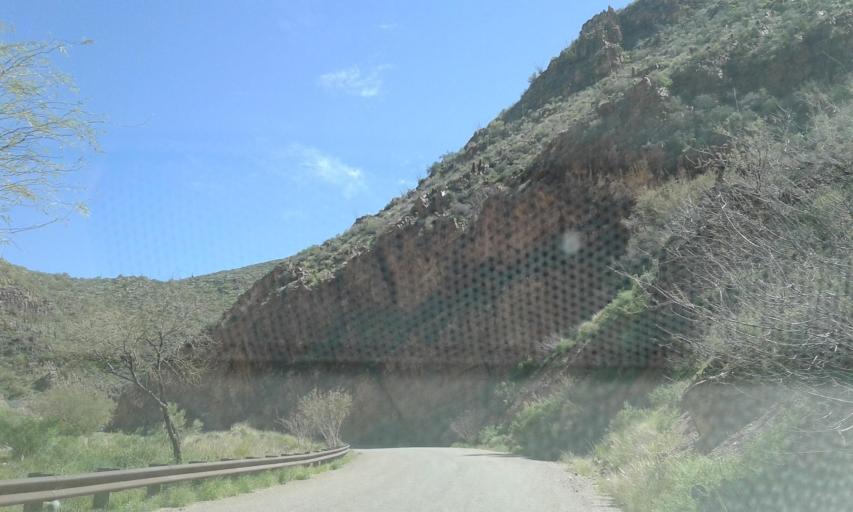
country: US
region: Arizona
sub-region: Gila County
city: Tonto Basin
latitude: 33.6683
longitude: -111.1630
